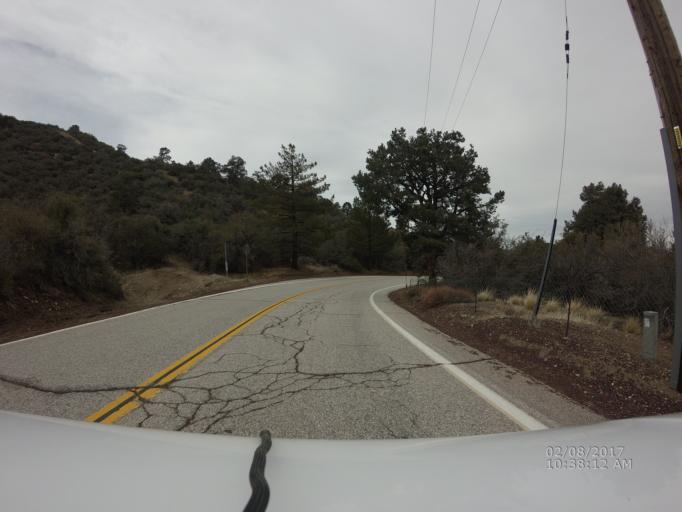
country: US
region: California
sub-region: San Bernardino County
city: Pinon Hills
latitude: 34.4091
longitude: -117.7696
